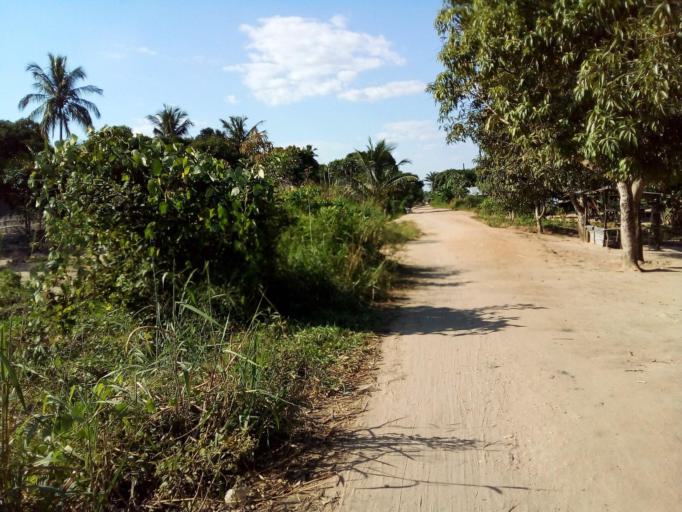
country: MZ
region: Zambezia
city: Quelimane
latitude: -17.5993
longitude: 36.8261
